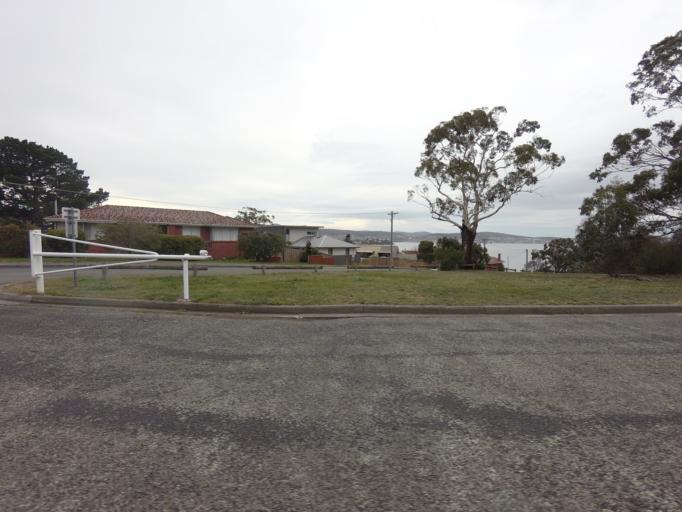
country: AU
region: Tasmania
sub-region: Clarence
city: Bellerive
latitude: -42.8807
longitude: 147.3675
